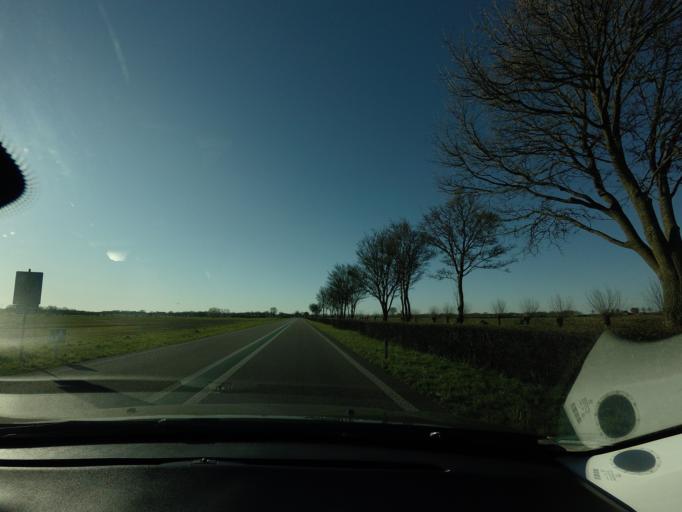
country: NL
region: Gelderland
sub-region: Gemeente Culemborg
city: Culemborg
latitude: 51.9469
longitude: 5.2738
